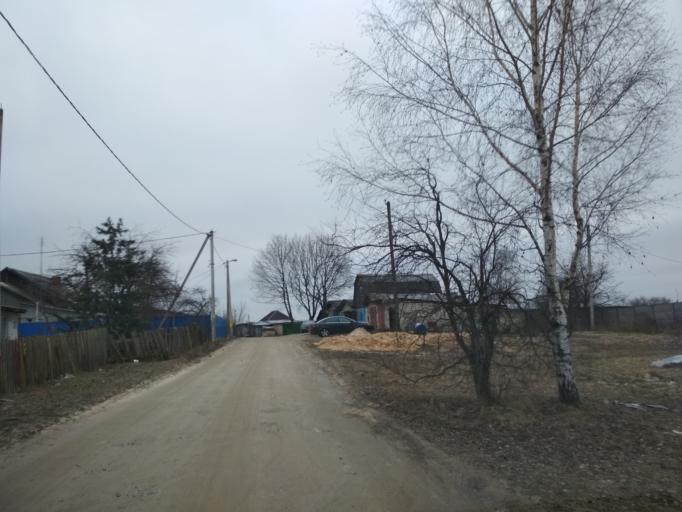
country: BY
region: Minsk
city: Mar''ina Horka
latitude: 53.5033
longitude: 28.1531
